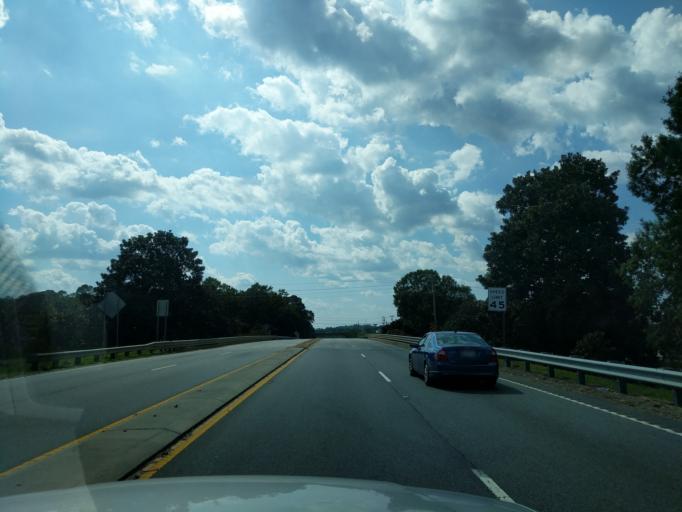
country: US
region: South Carolina
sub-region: Pickens County
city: Easley
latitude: 34.8186
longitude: -82.6005
